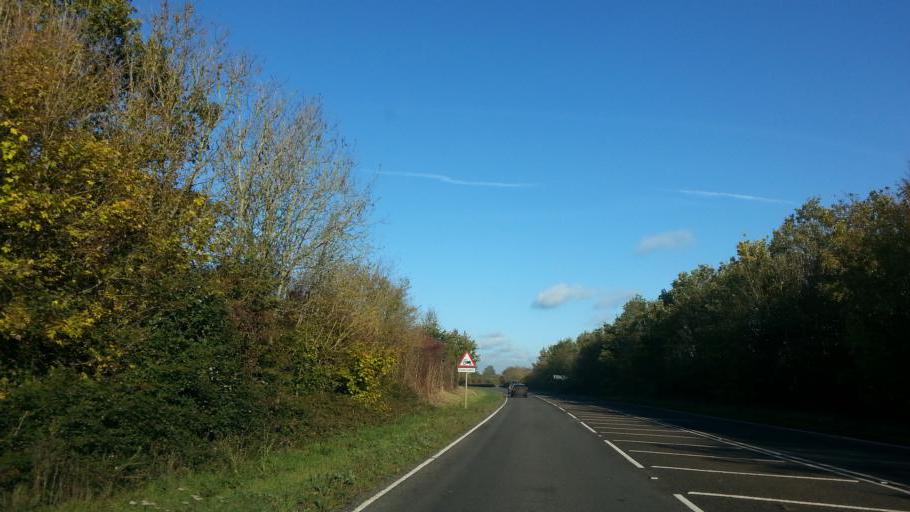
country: GB
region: England
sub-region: Norfolk
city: Harleston
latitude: 52.3978
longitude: 1.3111
